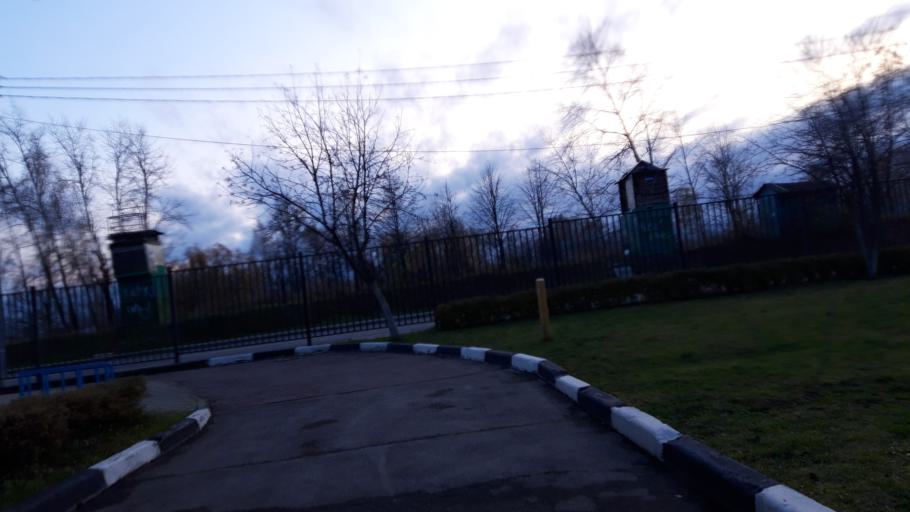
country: RU
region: Moscow
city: Zelenograd
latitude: 55.9749
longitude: 37.1897
